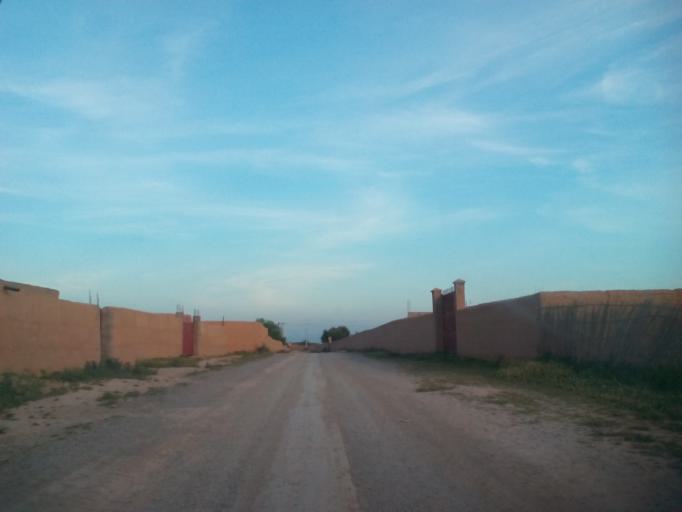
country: MA
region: Marrakech-Tensift-Al Haouz
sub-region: Marrakech
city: Marrakesh
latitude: 31.6273
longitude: -8.2866
